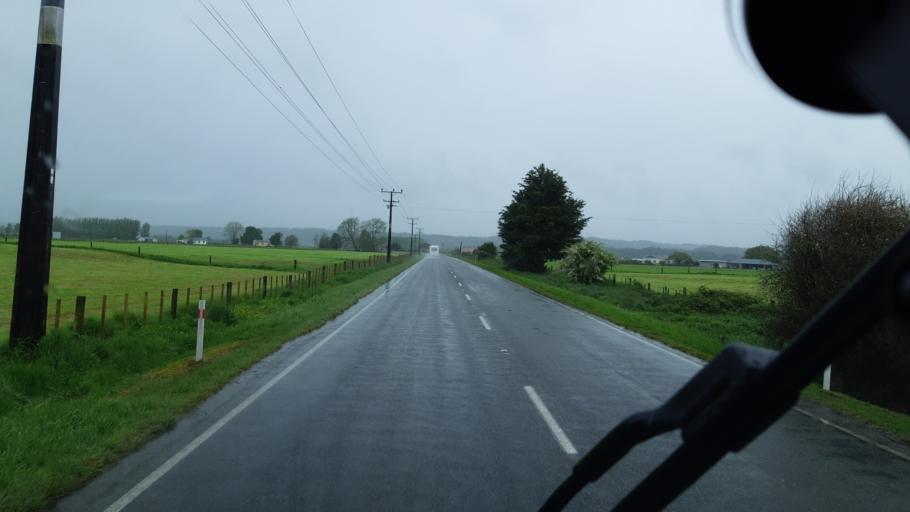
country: NZ
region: West Coast
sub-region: Grey District
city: Greymouth
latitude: -42.2940
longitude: 171.6317
